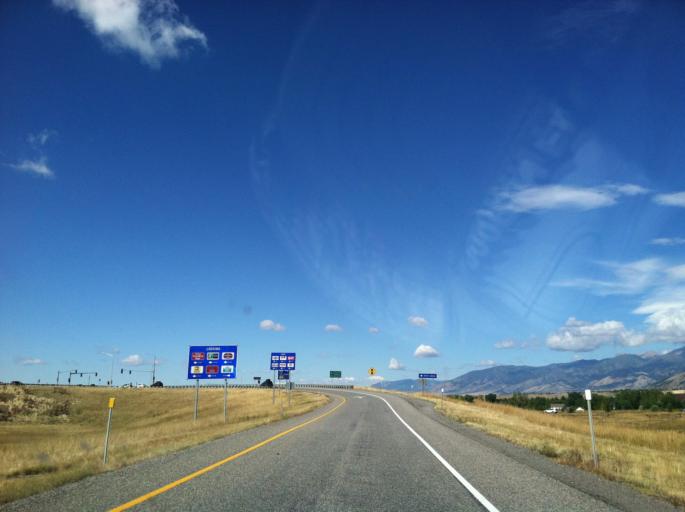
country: US
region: Montana
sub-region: Gallatin County
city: Bozeman
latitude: 45.7104
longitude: -111.0614
